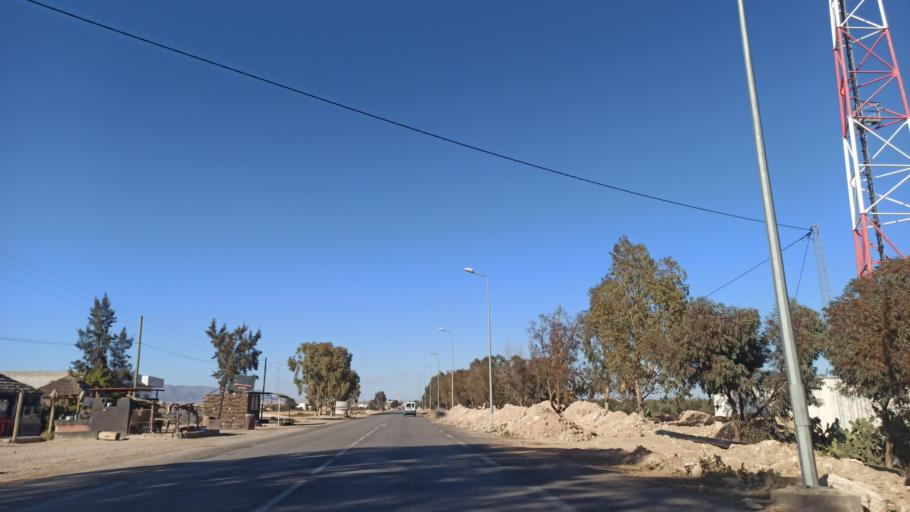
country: TN
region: Sidi Bu Zayd
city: Jilma
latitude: 35.2920
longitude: 9.4174
